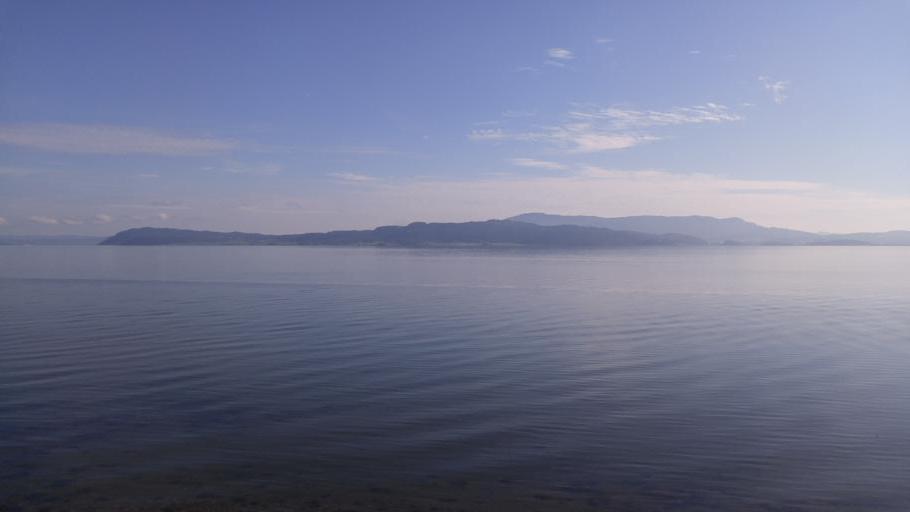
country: NO
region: Sor-Trondelag
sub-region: Malvik
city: Hommelvik
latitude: 63.4312
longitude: 10.7635
